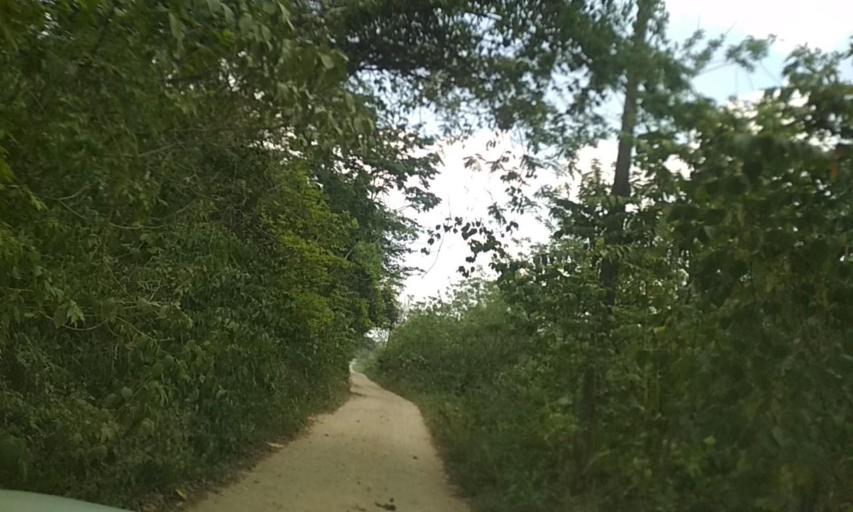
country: MX
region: Chiapas
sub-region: Tecpatan
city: Raudales Malpaso
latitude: 17.2861
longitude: -93.8388
